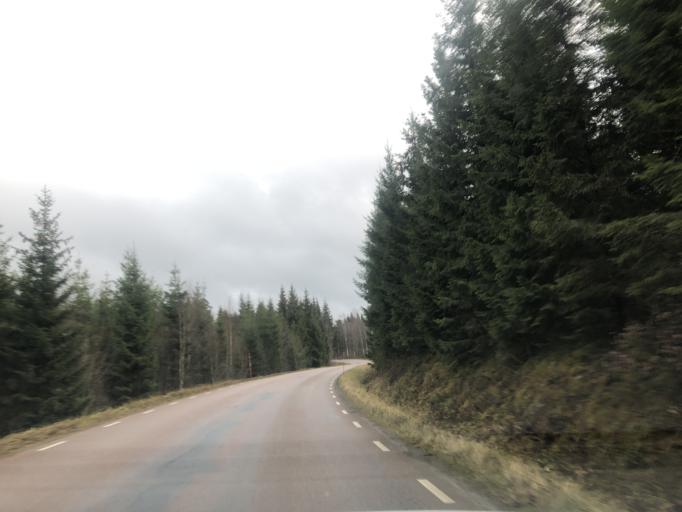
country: SE
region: Vaestra Goetaland
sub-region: Ulricehamns Kommun
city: Ulricehamn
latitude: 57.8324
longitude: 13.4824
